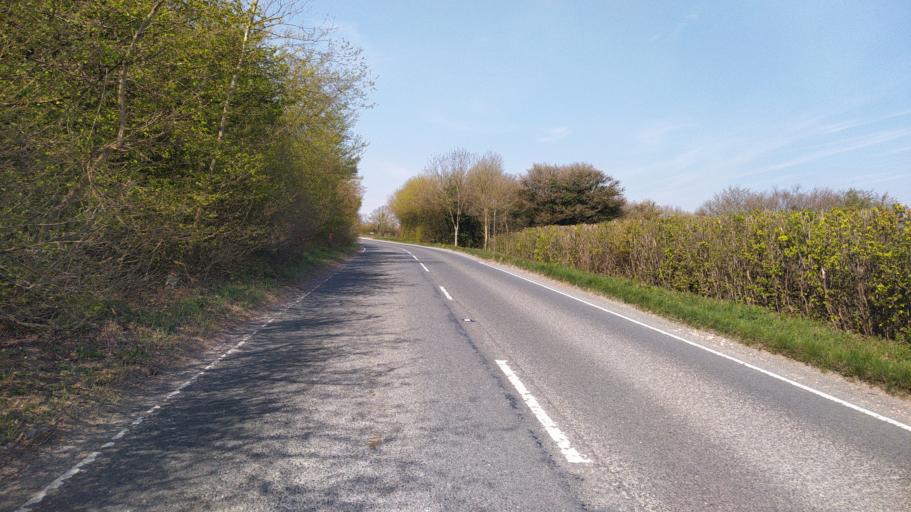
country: GB
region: England
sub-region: Somerset
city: Frome
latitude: 51.2132
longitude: -2.3951
